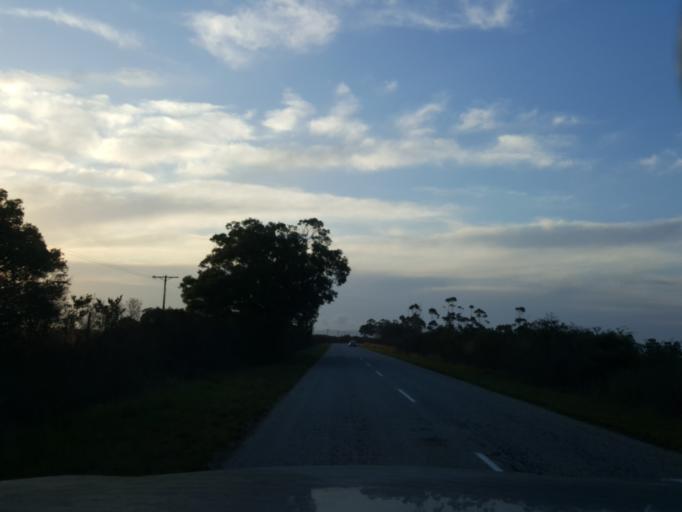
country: ZA
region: Eastern Cape
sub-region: Cacadu District Municipality
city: Grahamstown
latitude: -33.4434
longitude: 26.4844
